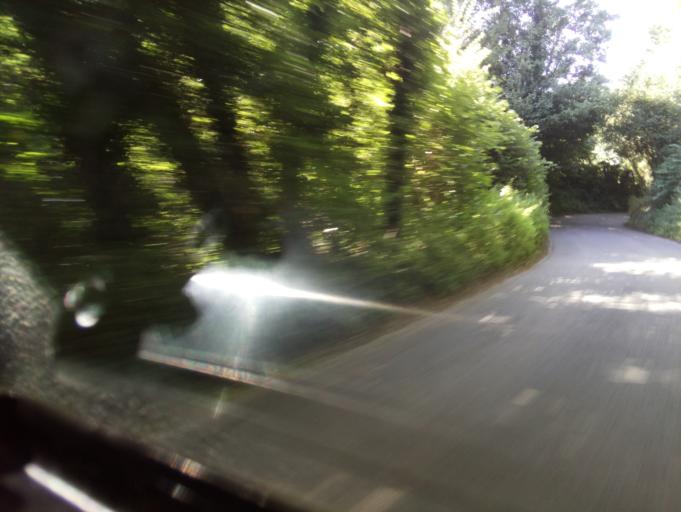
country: GB
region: England
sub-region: Herefordshire
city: Ross on Wye
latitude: 51.9281
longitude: -2.5790
